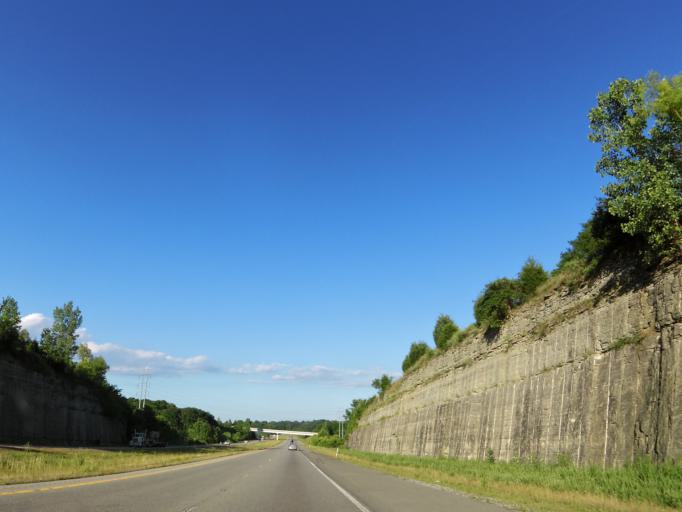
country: US
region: Tennessee
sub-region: Williamson County
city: Nolensville
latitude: 35.8413
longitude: -86.6357
